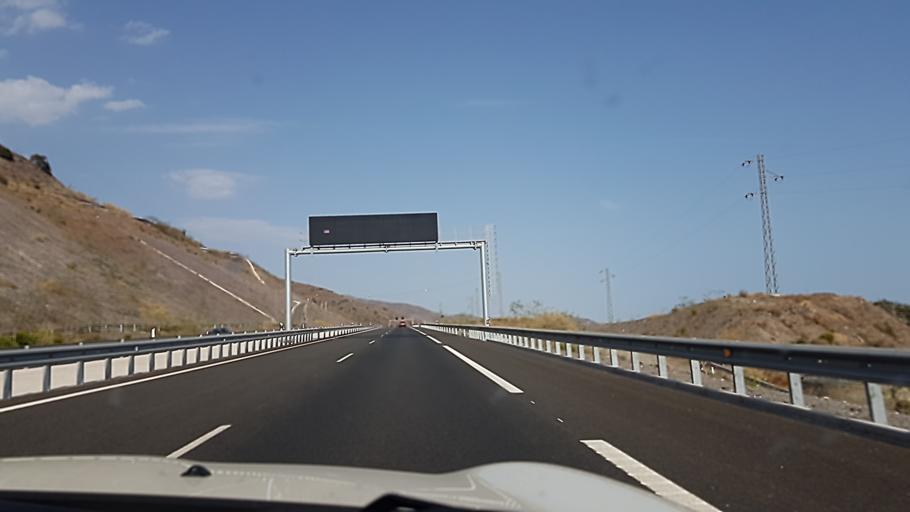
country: ES
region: Andalusia
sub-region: Provincia de Granada
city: Sorvilan
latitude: 36.7540
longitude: -3.2686
